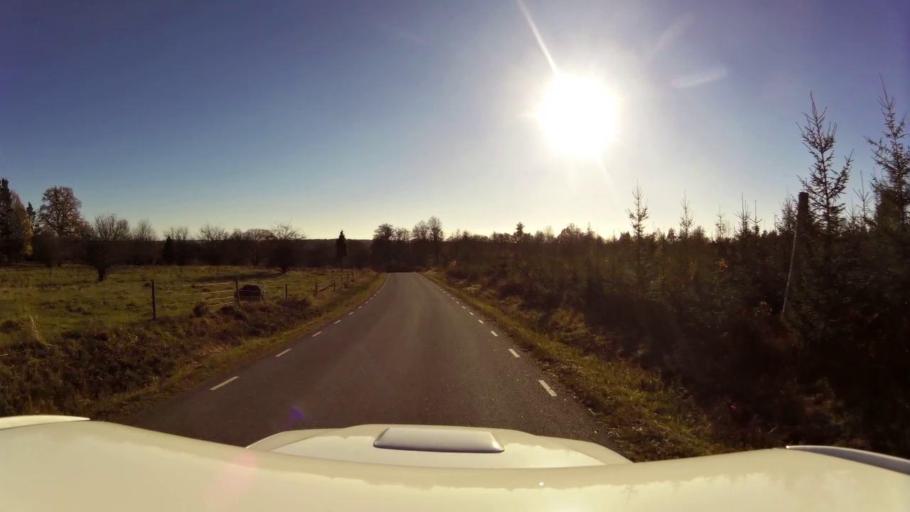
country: SE
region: OEstergoetland
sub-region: Linkopings Kommun
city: Sturefors
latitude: 58.2687
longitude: 15.6648
